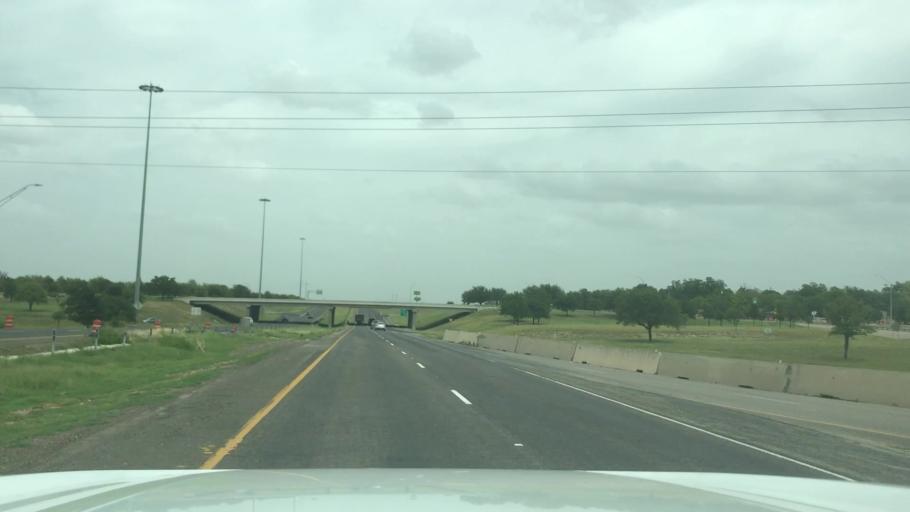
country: US
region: Texas
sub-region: McLennan County
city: Beverly
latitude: 31.4974
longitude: -97.1274
